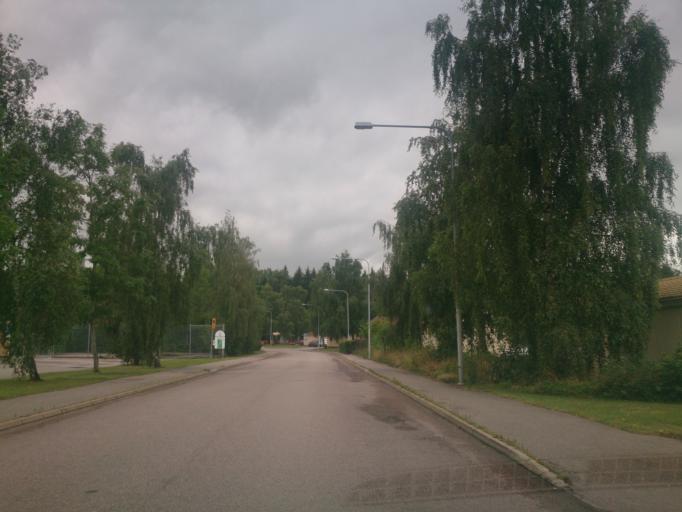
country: SE
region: OEstergoetland
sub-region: Linkopings Kommun
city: Malmslatt
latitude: 58.4189
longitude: 15.4991
